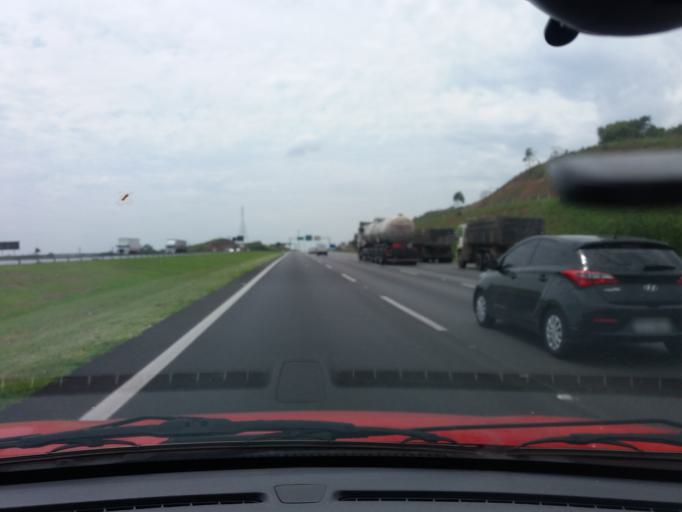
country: BR
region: Sao Paulo
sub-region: Osasco
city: Osasco
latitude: -23.4464
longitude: -46.7797
